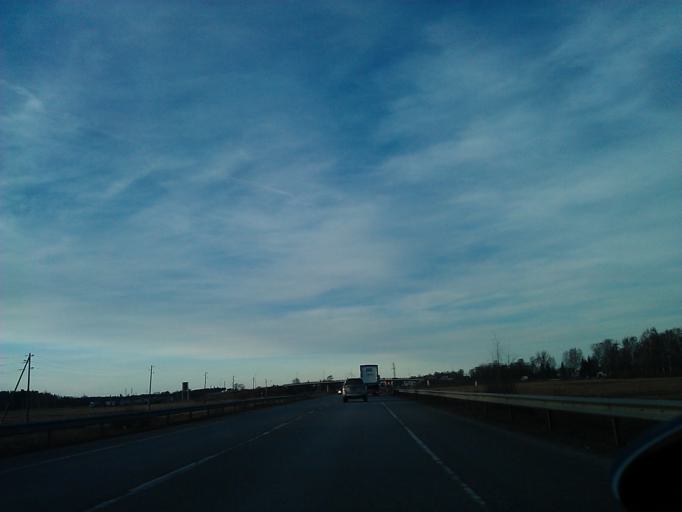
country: LV
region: Adazi
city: Adazi
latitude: 57.0642
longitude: 24.3212
